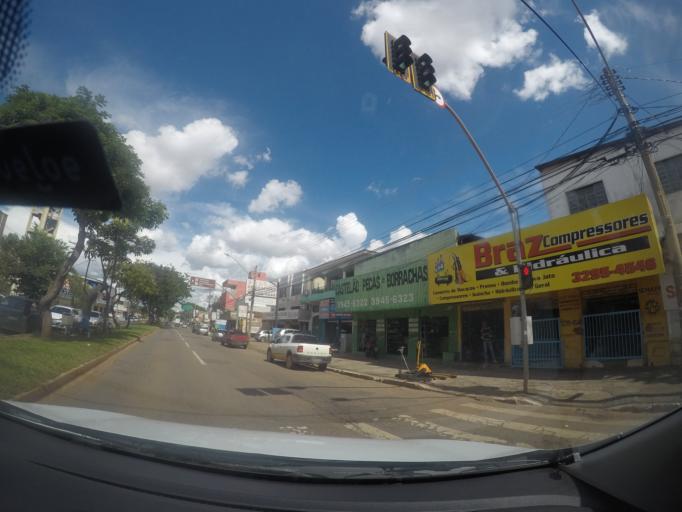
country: BR
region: Goias
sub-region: Goiania
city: Goiania
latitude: -16.6711
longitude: -49.3071
